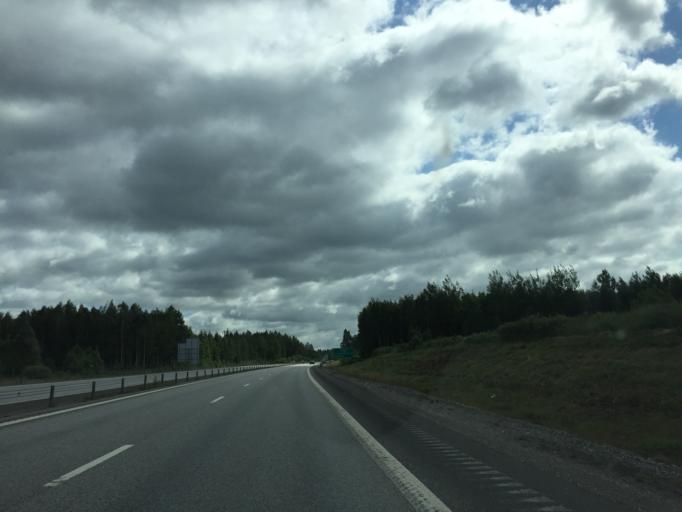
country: SE
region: OErebro
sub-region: Orebro Kommun
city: Vintrosa
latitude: 59.2477
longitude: 15.0706
